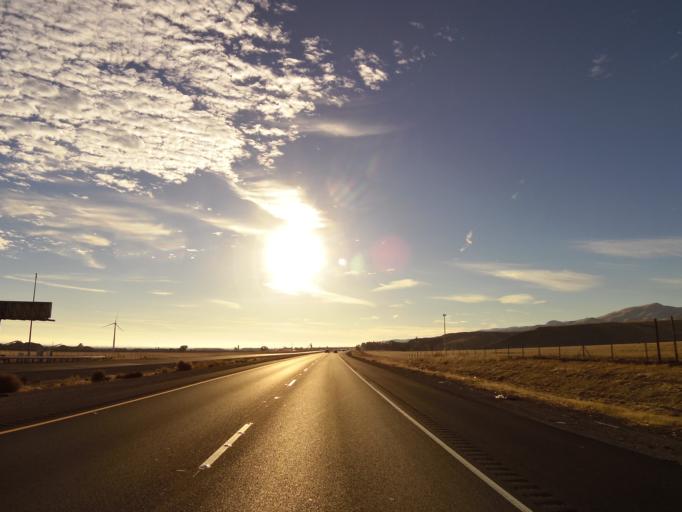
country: US
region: California
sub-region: San Joaquin County
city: Tracy
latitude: 37.6208
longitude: -121.3729
